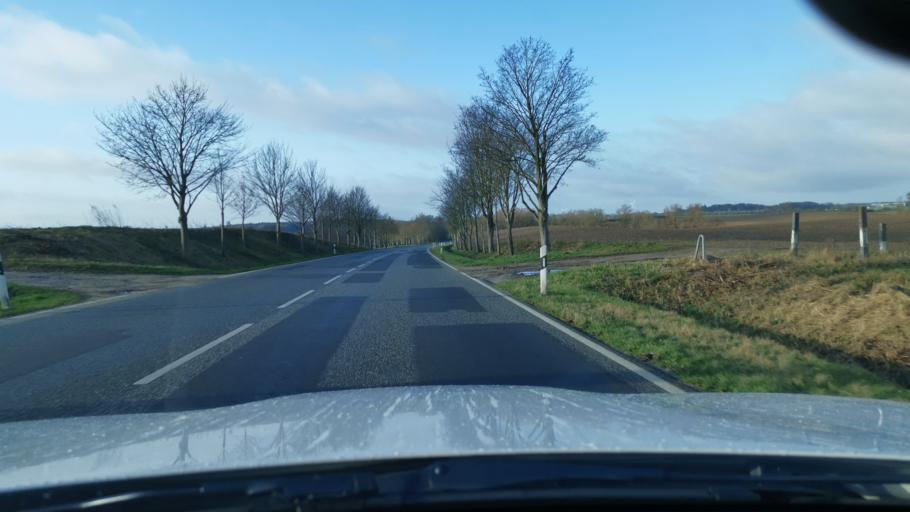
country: DE
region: Mecklenburg-Vorpommern
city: Laage
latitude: 53.9073
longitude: 12.3112
